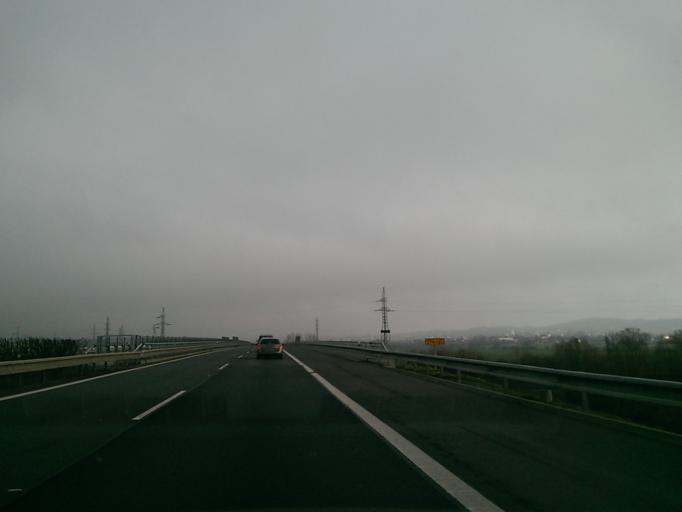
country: CZ
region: Olomoucky
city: Grygov
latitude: 49.5561
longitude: 17.2931
